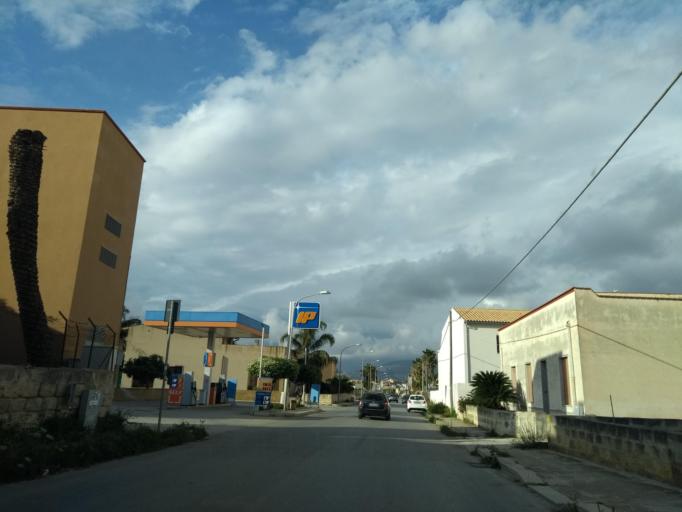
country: IT
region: Sicily
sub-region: Trapani
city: Marausa
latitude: 37.9428
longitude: 12.5108
